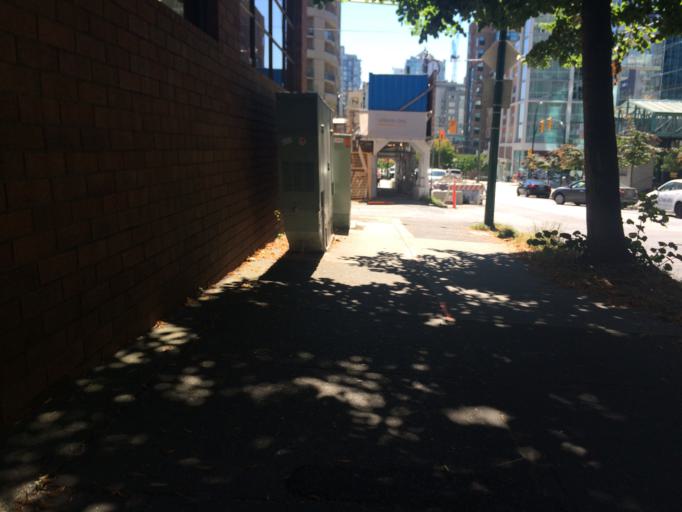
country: CA
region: British Columbia
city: West End
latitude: 49.2772
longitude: -123.1297
